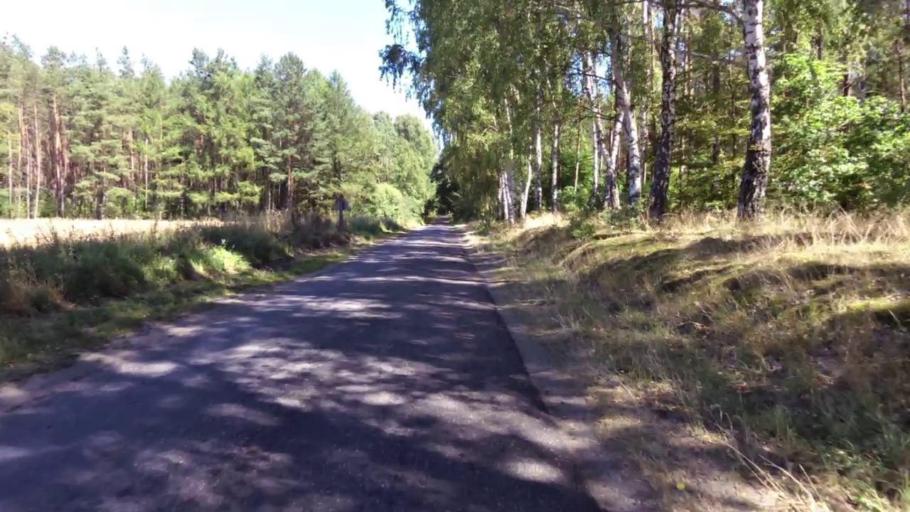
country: PL
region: West Pomeranian Voivodeship
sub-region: Powiat szczecinecki
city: Szczecinek
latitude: 53.6346
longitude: 16.6992
